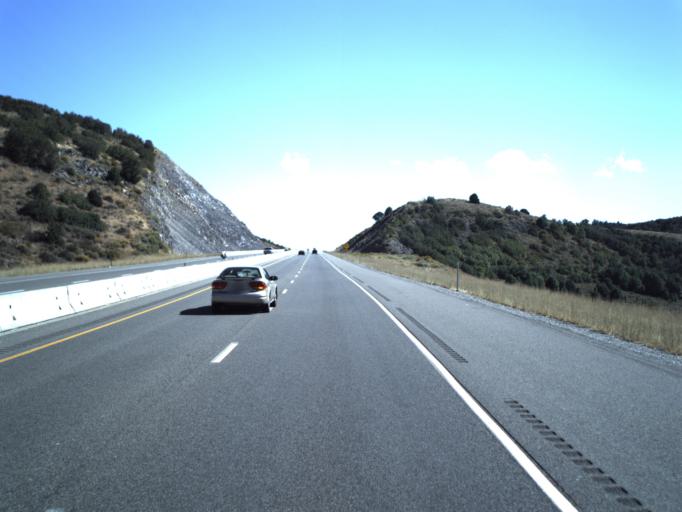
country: US
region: Utah
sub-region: Box Elder County
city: Brigham City
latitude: 41.5615
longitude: -111.9624
